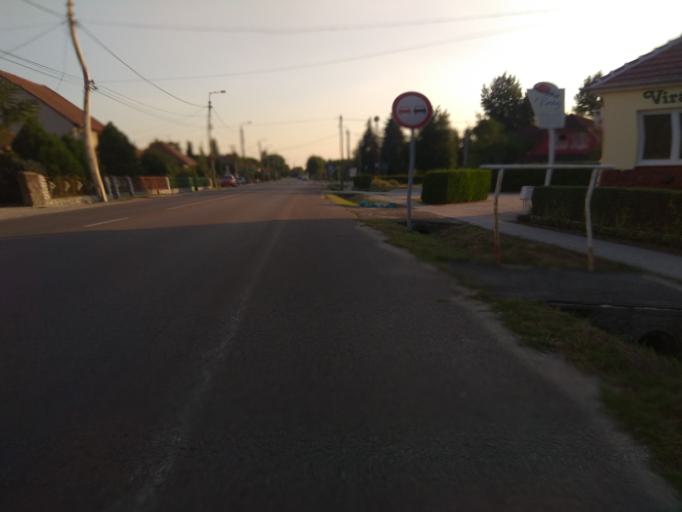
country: HU
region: Borsod-Abauj-Zemplen
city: Emod
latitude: 47.9341
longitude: 20.8180
